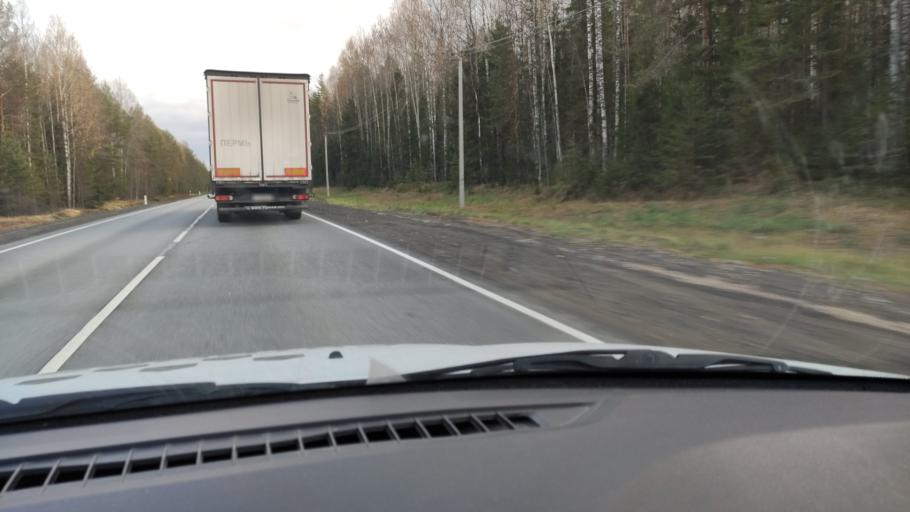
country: RU
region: Kirov
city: Dubrovka
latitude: 58.9111
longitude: 51.1724
